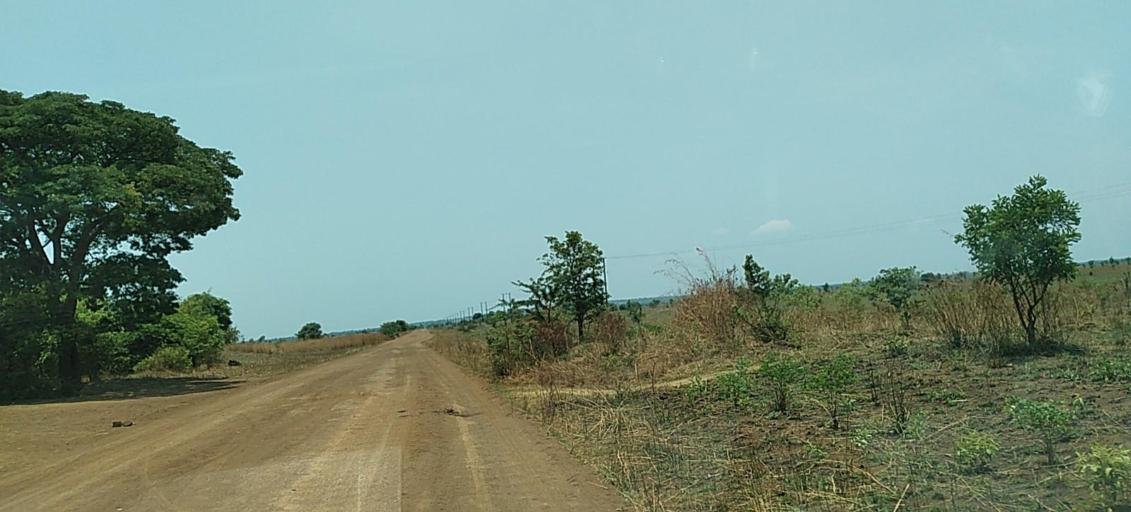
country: ZM
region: Copperbelt
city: Mpongwe
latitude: -13.6714
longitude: 27.8547
